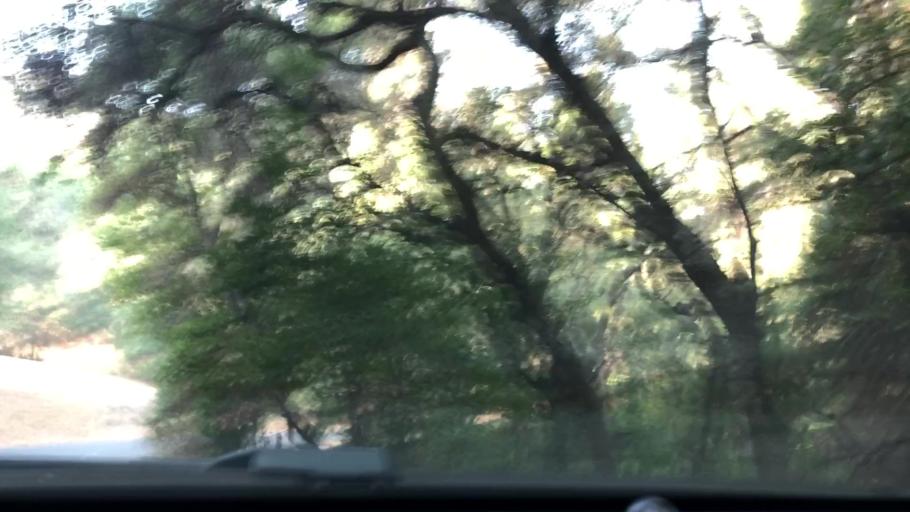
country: US
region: California
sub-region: Contra Costa County
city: Orinda
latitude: 37.9179
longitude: -122.1598
